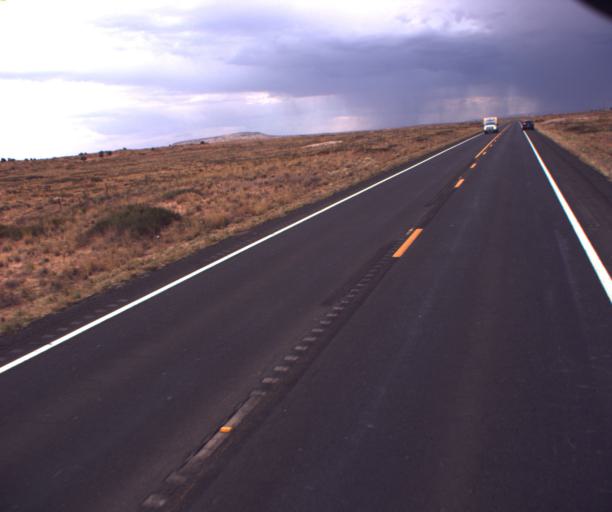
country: US
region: Arizona
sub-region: Coconino County
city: Tuba City
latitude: 36.2961
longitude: -110.9835
